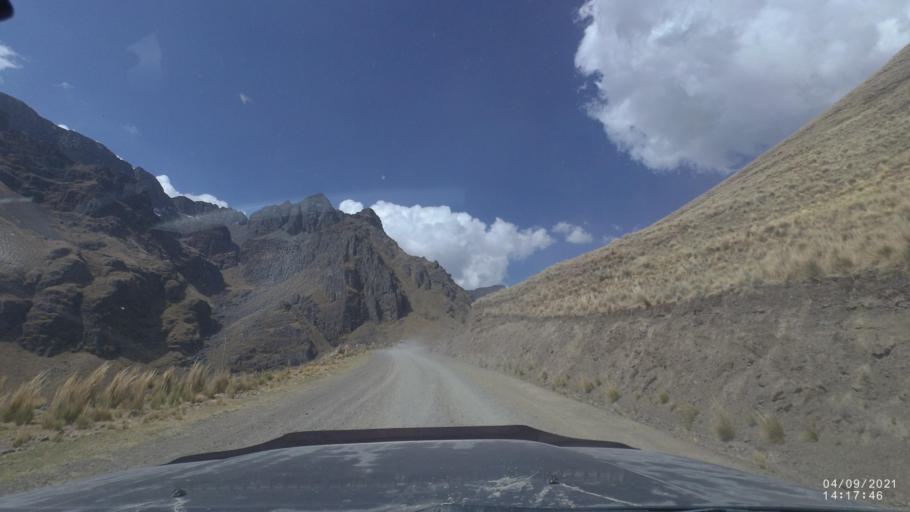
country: BO
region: Cochabamba
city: Sipe Sipe
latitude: -17.2305
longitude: -66.4330
